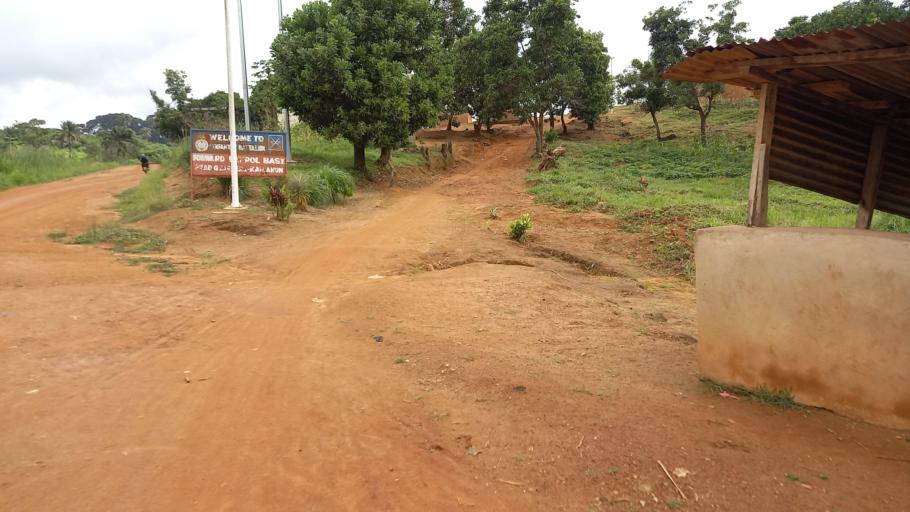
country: SL
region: Eastern Province
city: Kailahun
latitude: 8.2938
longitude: -10.5763
